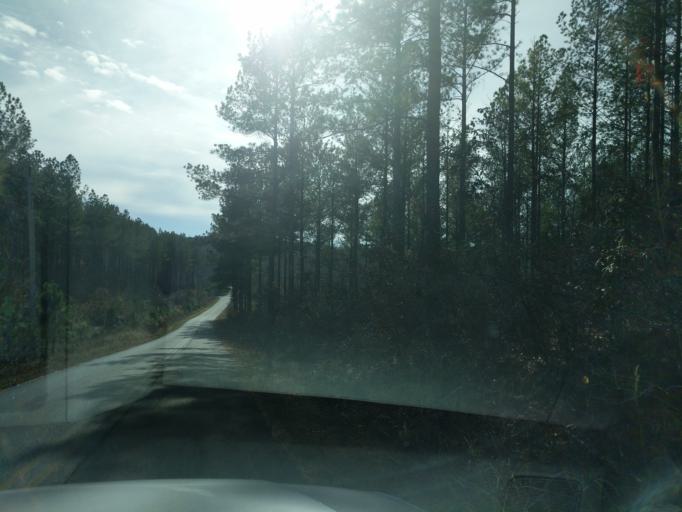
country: US
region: South Carolina
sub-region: Oconee County
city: Walhalla
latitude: 34.8545
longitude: -83.0536
